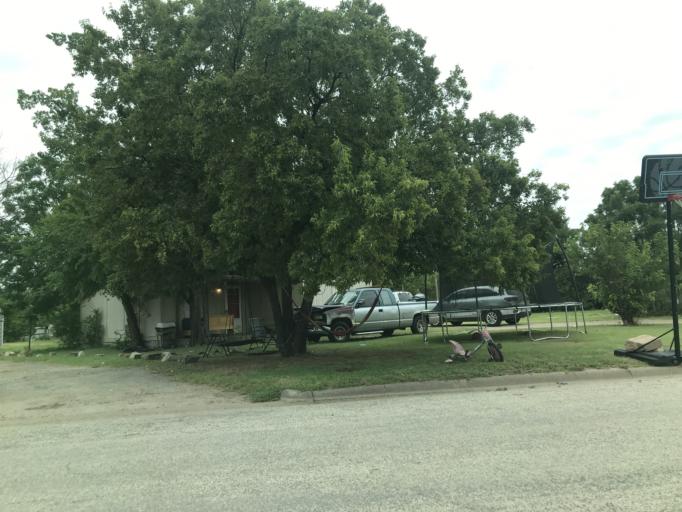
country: US
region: Texas
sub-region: Taylor County
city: Abilene
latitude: 32.4396
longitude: -99.7359
